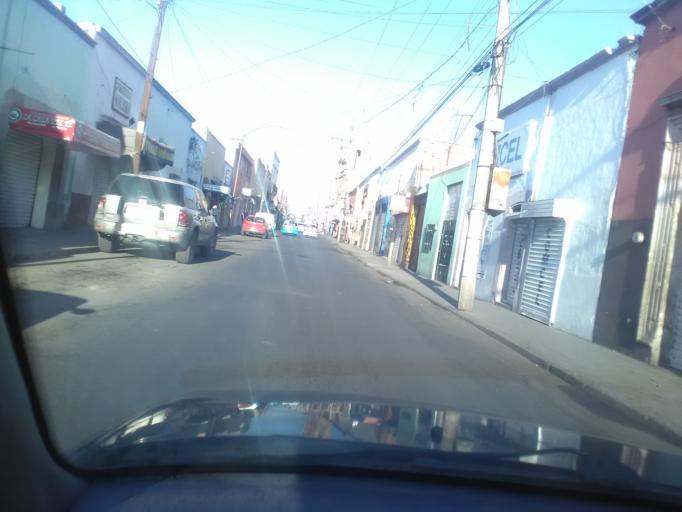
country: MX
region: Durango
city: Victoria de Durango
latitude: 24.0224
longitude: -104.6679
